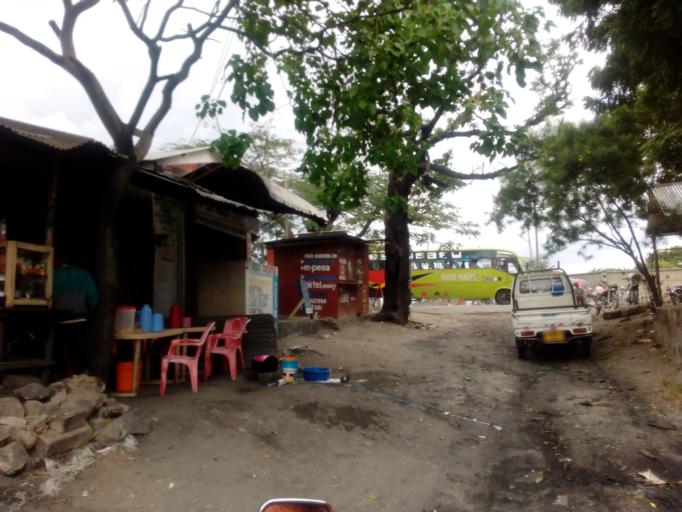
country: TZ
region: Dar es Salaam
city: Dar es Salaam
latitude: -6.8526
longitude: 39.2530
